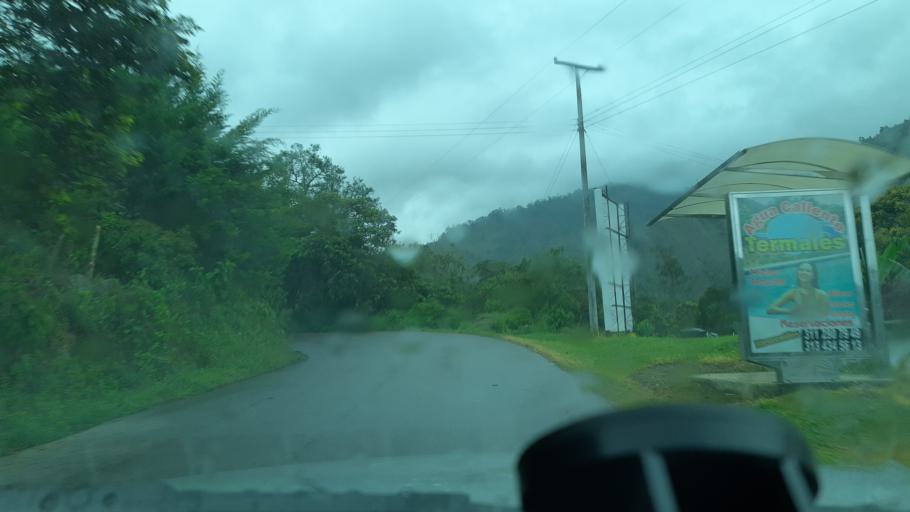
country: CO
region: Boyaca
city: Chinavita
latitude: 5.2051
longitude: -73.3882
